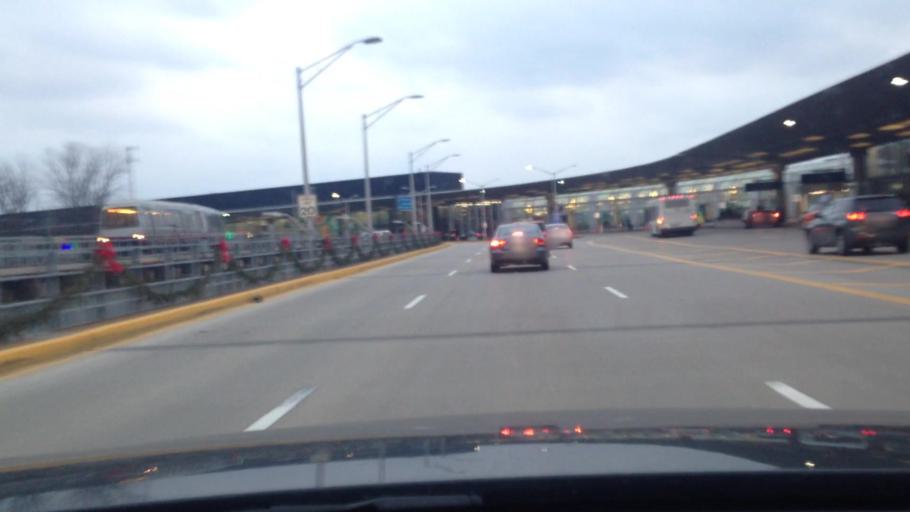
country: US
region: Illinois
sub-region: Cook County
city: Rosemont
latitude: 41.9787
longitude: -87.9059
